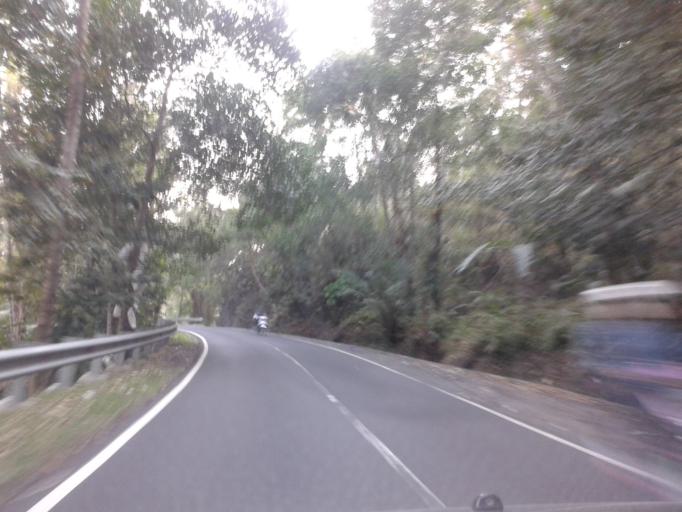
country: ID
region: Bali
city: Banjar Wangsian
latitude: -8.4812
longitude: 115.3991
